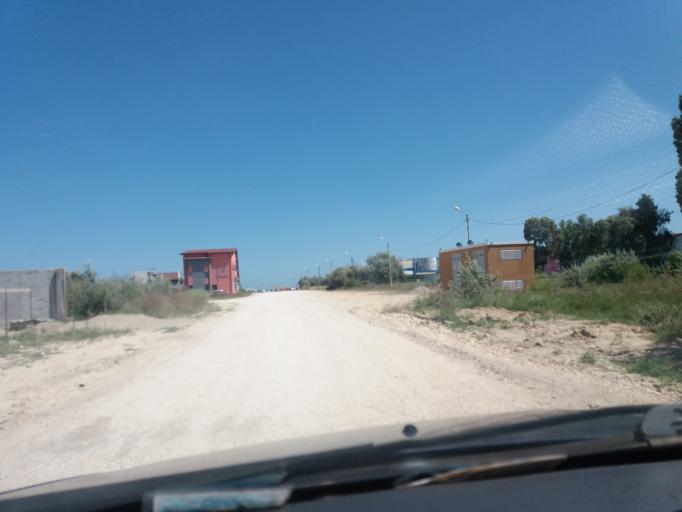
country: RO
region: Constanta
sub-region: Comuna Navodari
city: Navodari
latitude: 44.3210
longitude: 28.6313
